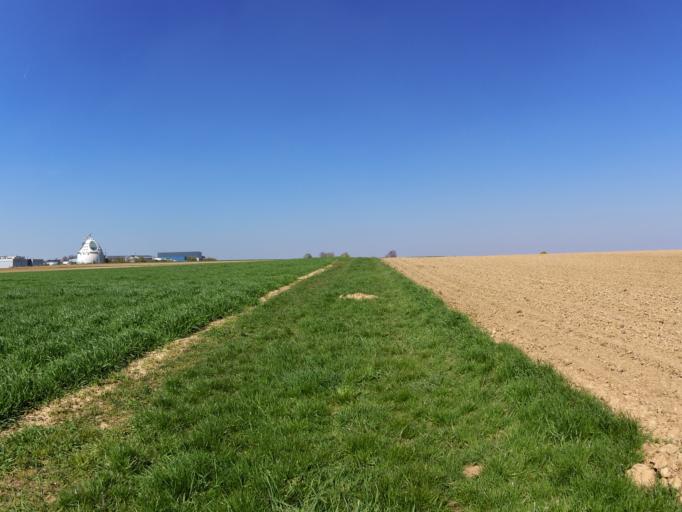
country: DE
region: Bavaria
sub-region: Regierungsbezirk Unterfranken
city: Biebelried
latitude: 49.7749
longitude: 10.0764
